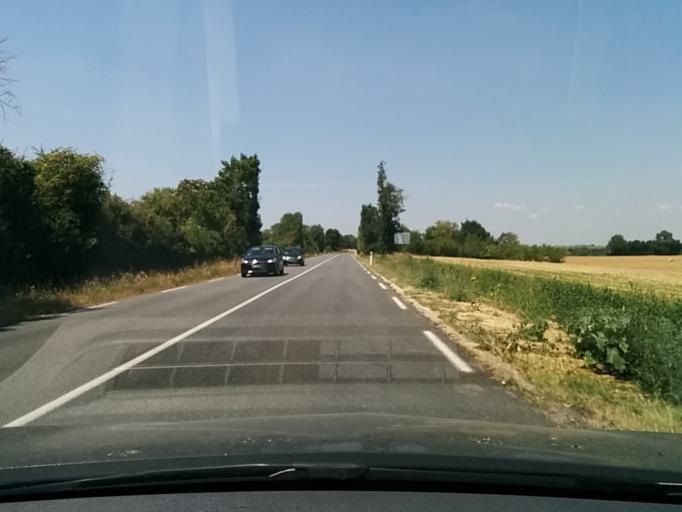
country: FR
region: Midi-Pyrenees
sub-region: Departement du Gers
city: Gimont
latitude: 43.6041
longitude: 0.9958
